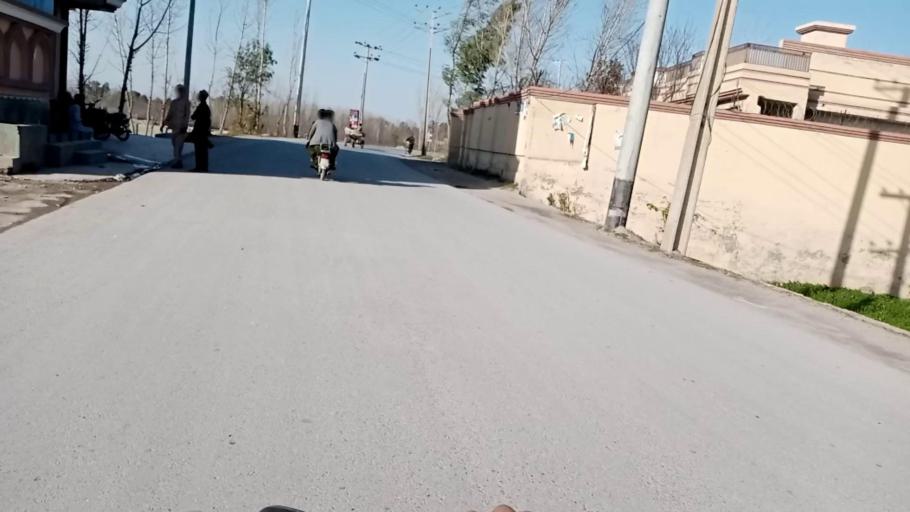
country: PK
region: Khyber Pakhtunkhwa
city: Peshawar
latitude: 34.0503
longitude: 71.5269
